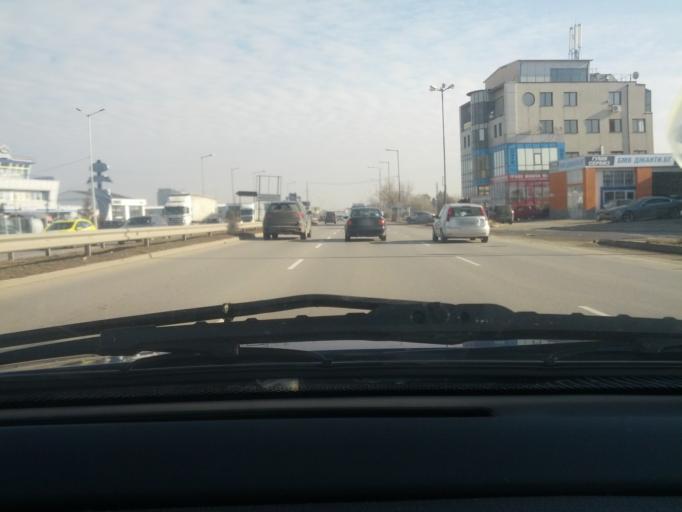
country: BG
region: Sofia-Capital
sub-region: Stolichna Obshtina
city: Sofia
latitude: 42.7091
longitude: 23.4283
